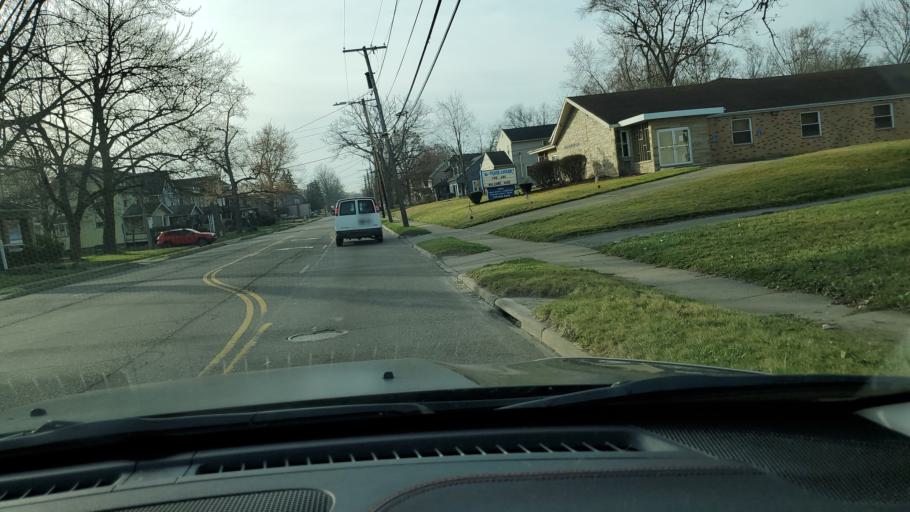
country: US
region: Ohio
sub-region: Trumbull County
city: Niles
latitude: 41.1910
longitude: -80.7683
